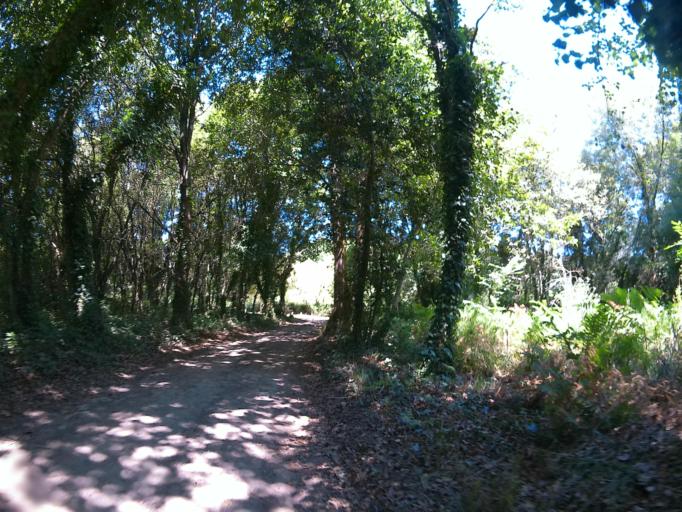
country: PT
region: Viana do Castelo
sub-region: Viana do Castelo
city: Darque
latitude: 41.7216
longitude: -8.7051
